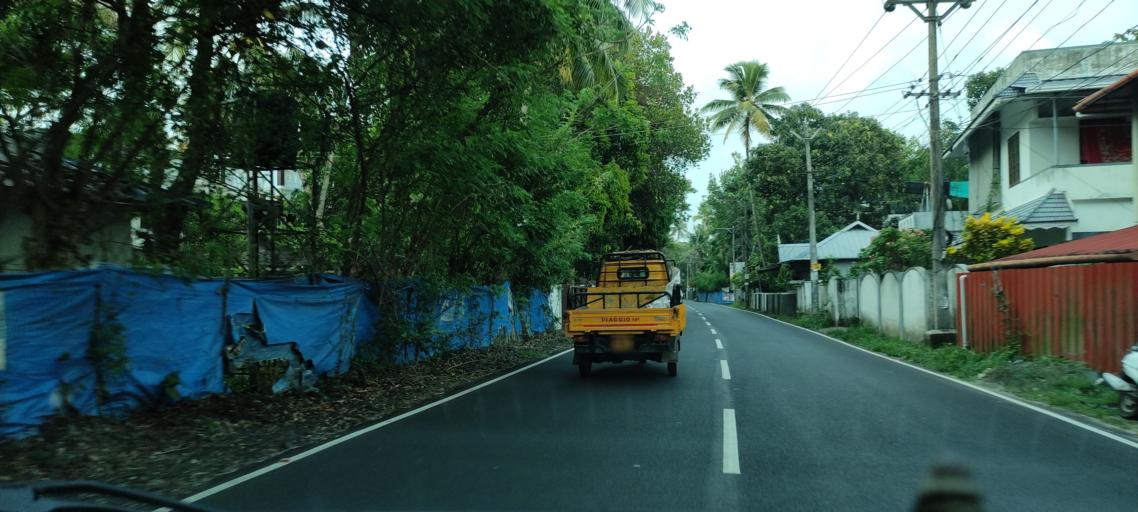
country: IN
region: Kerala
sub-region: Alappuzha
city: Kutiatodu
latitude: 9.8288
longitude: 76.3417
